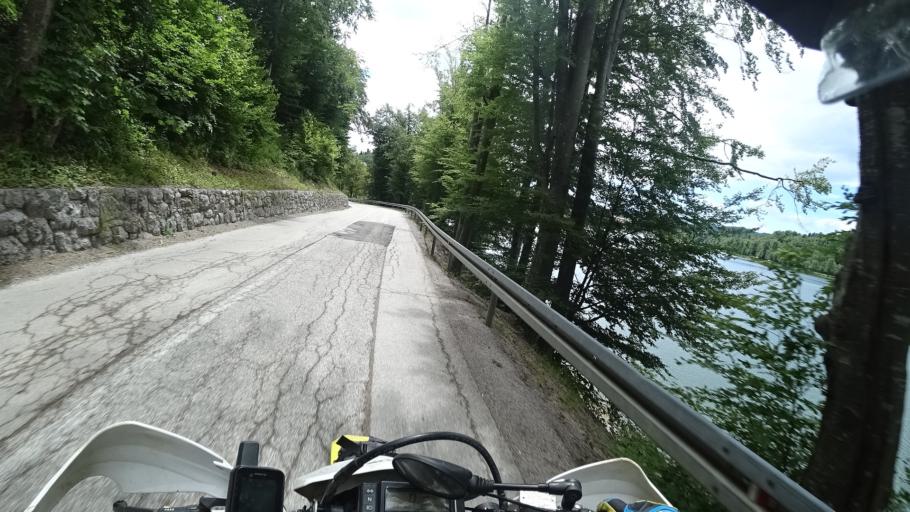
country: HR
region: Primorsko-Goranska
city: Hreljin
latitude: 45.3151
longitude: 14.7149
